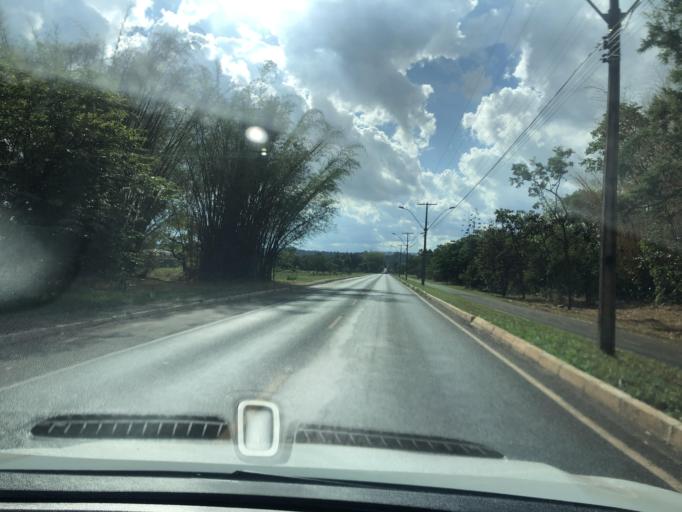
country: BR
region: Federal District
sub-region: Brasilia
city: Brasilia
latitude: -15.8984
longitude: -47.9289
